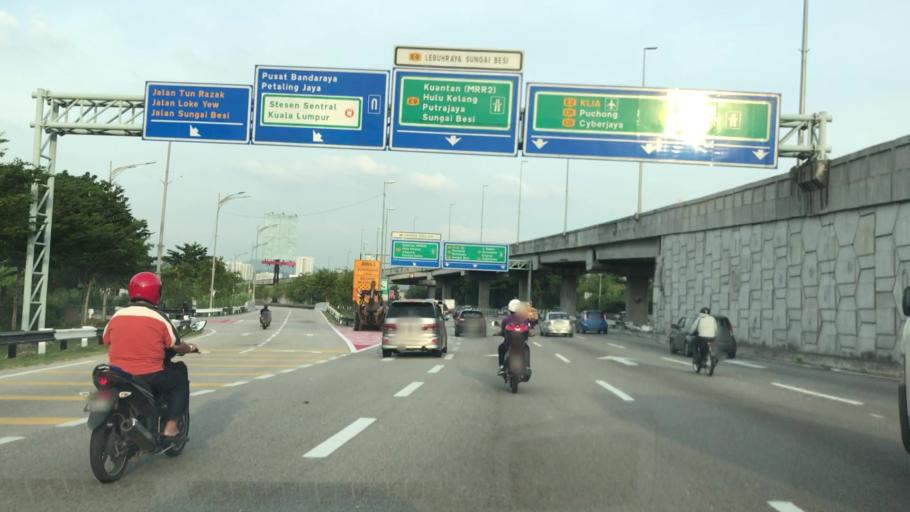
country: MY
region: Kuala Lumpur
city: Kuala Lumpur
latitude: 3.1231
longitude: 101.7047
